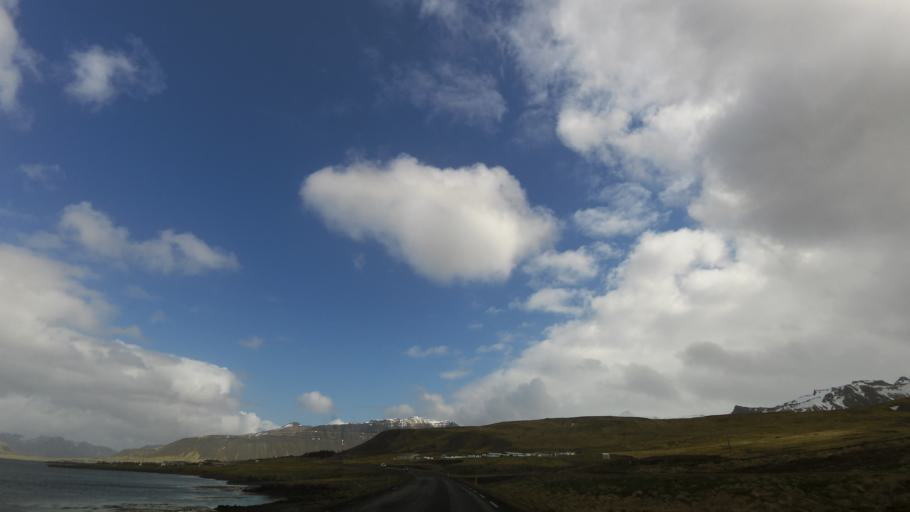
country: IS
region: West
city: Olafsvik
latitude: 64.9220
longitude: -23.2898
